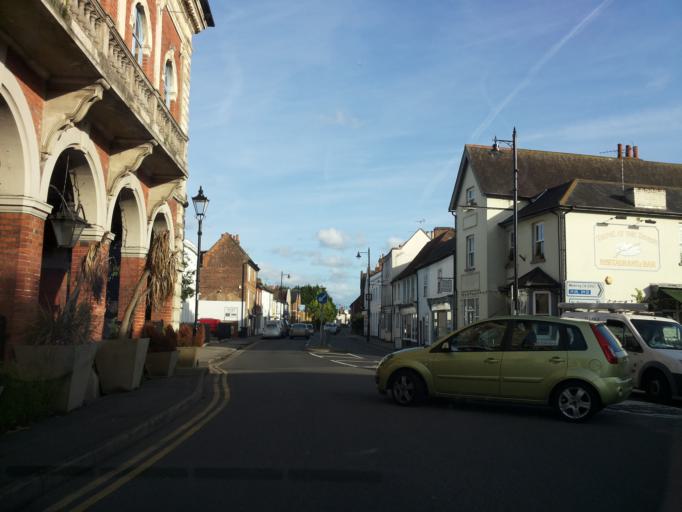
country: GB
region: England
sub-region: Surrey
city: Chertsey
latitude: 51.3920
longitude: -0.5030
